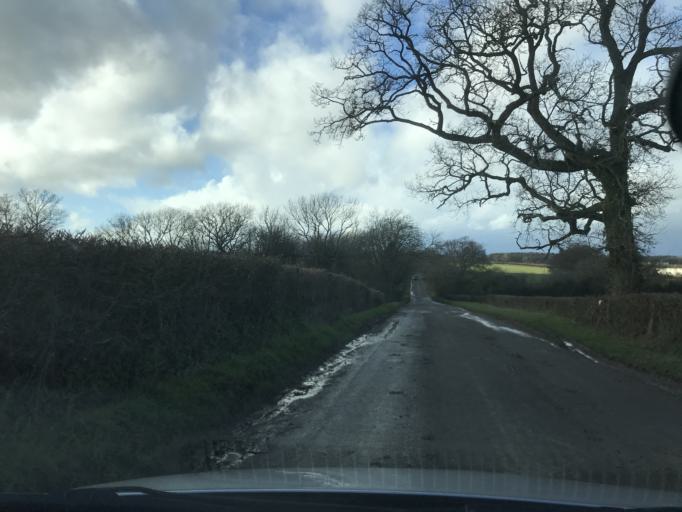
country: GB
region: England
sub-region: Somerset
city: Creech Saint Michael
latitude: 50.9553
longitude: -3.0160
